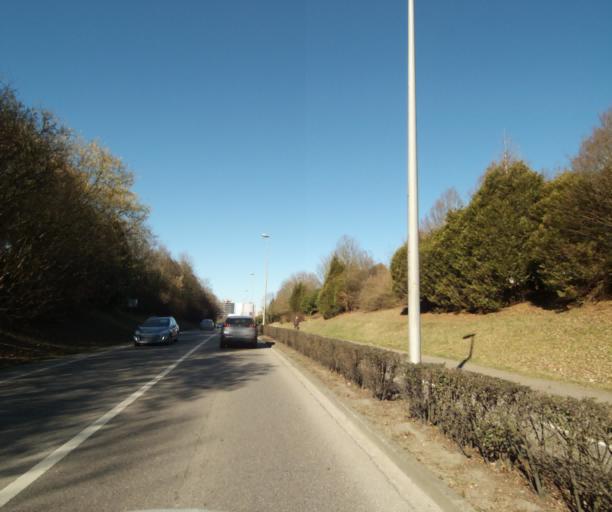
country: FR
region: Lorraine
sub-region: Departement de Meurthe-et-Moselle
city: Vandoeuvre-les-Nancy
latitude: 48.6559
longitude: 6.1789
